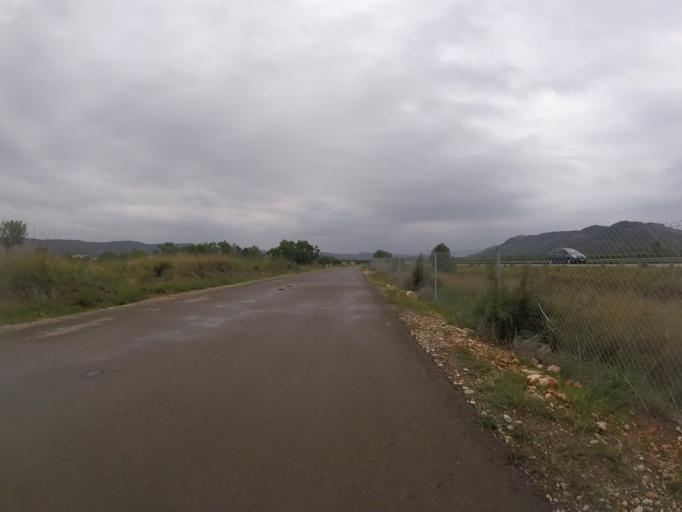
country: ES
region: Valencia
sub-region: Provincia de Castello
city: Alcala de Xivert
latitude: 40.2903
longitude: 0.2287
